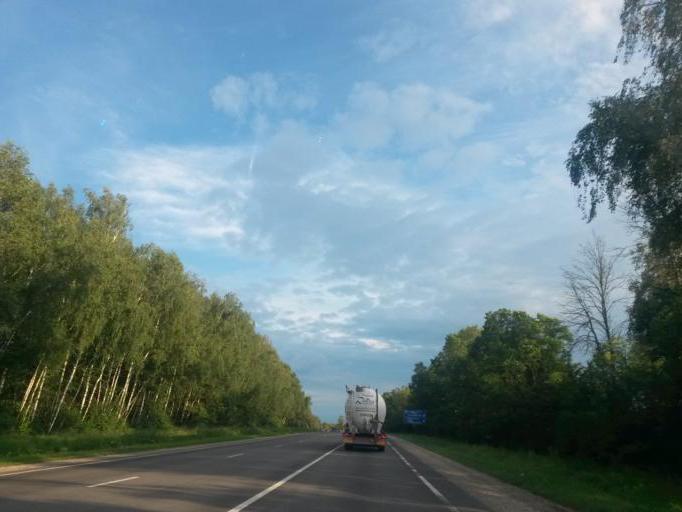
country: RU
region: Moskovskaya
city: Barybino
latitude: 55.2081
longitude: 37.8683
